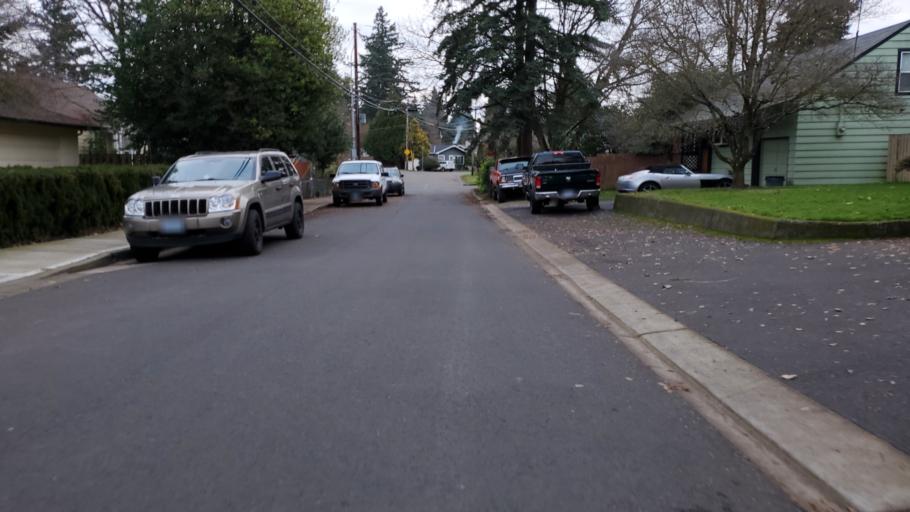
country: US
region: Oregon
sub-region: Clackamas County
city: Gladstone
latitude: 45.3860
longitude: -122.6022
